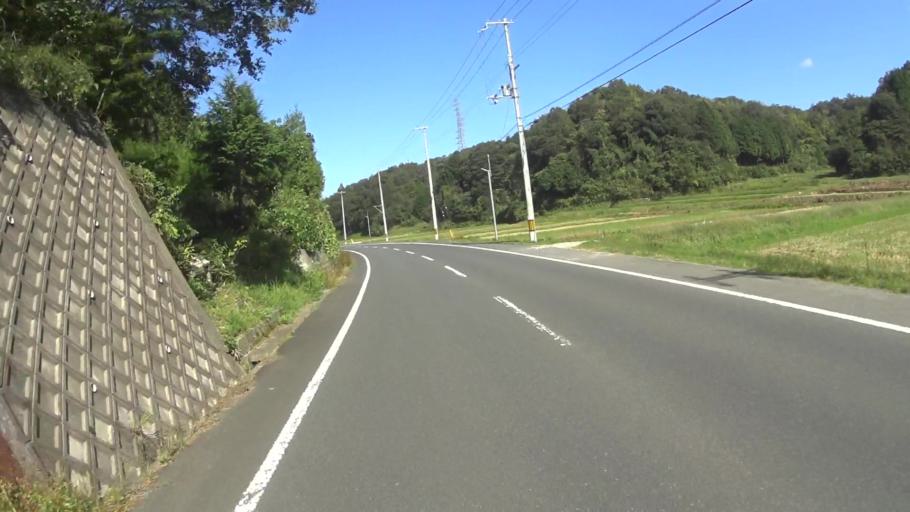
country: JP
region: Kyoto
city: Miyazu
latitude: 35.6654
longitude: 135.0598
